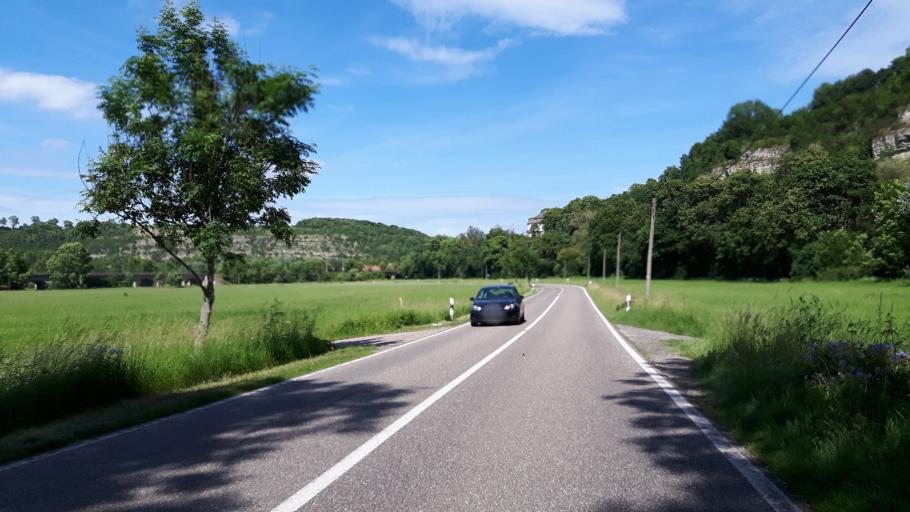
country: DE
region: Thuringia
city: Grossheringen
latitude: 51.1073
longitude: 11.6932
